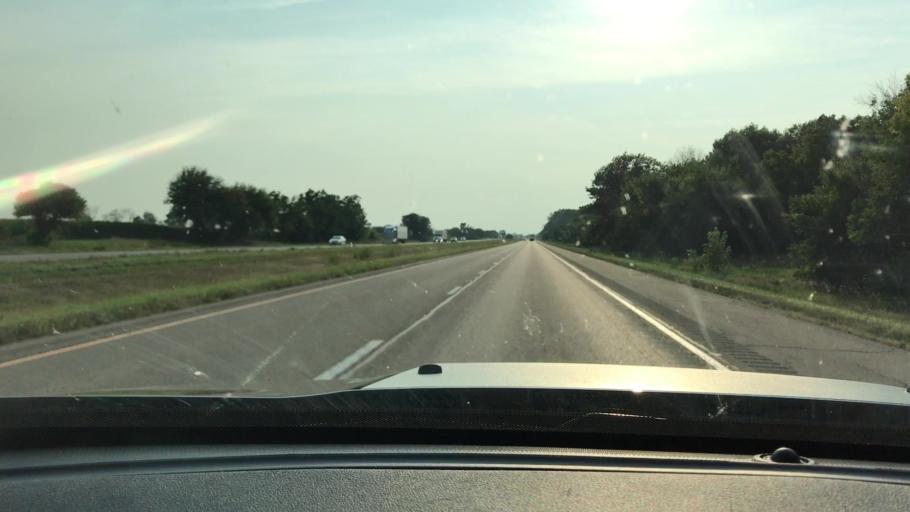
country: US
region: Illinois
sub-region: Henry County
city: Kewanee
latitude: 41.3865
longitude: -89.7753
